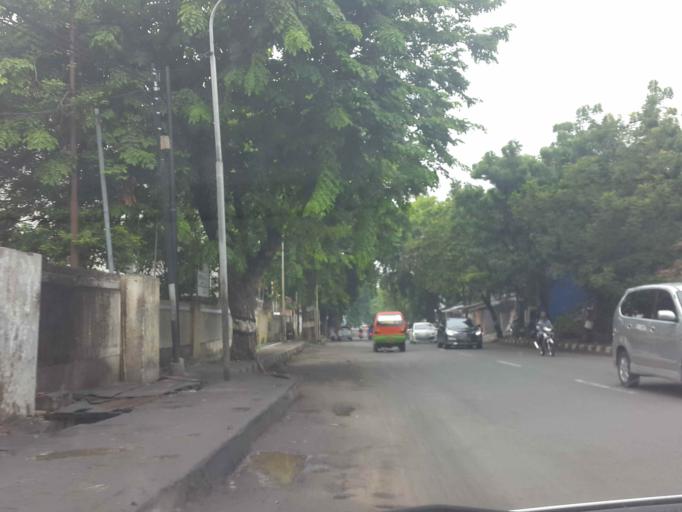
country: ID
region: Central Java
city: Semarang
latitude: -6.9934
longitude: 110.4134
